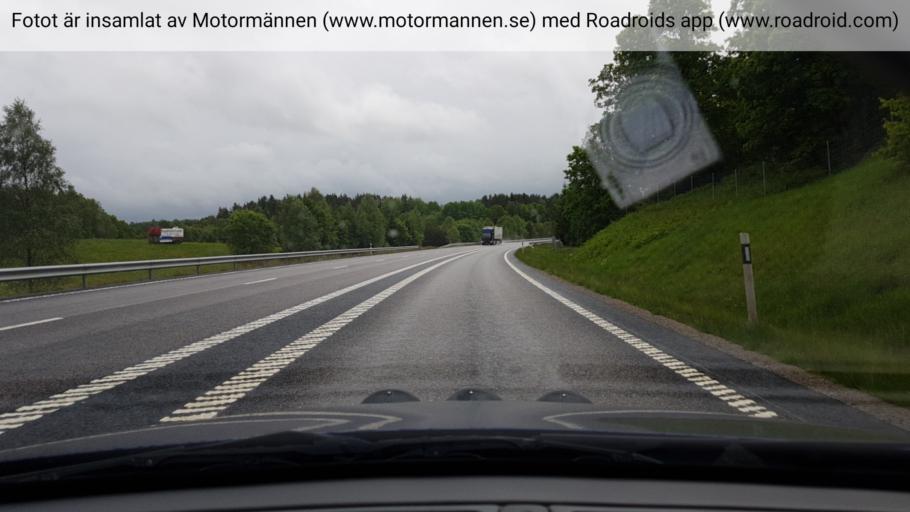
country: SE
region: Vaestra Goetaland
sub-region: Boras Kommun
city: Viskafors
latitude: 57.6031
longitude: 12.8732
